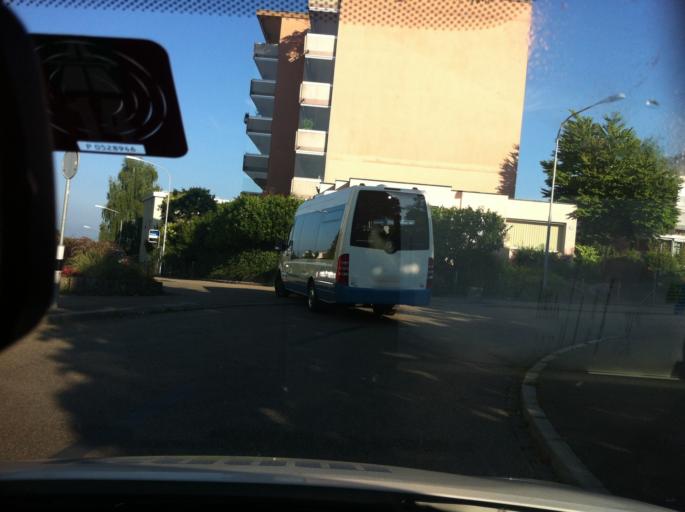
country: CH
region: Zurich
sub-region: Bezirk Meilen
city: Zollikerberg
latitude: 47.3539
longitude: 8.6015
